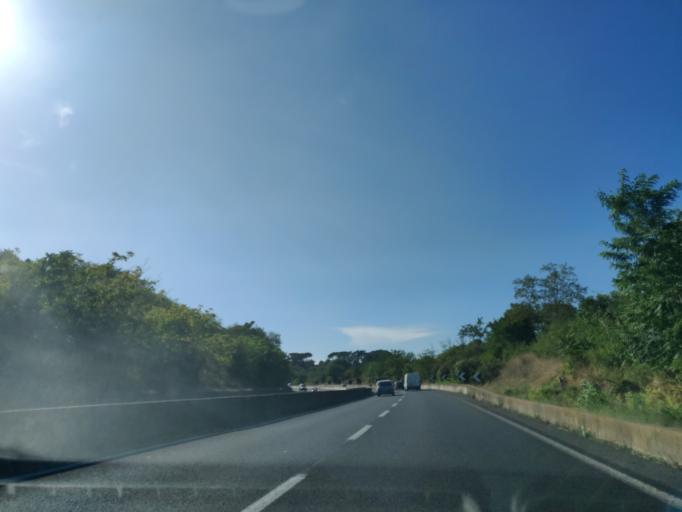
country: IT
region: Latium
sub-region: Citta metropolitana di Roma Capitale
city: Ara Nova
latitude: 41.9093
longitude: 12.2613
